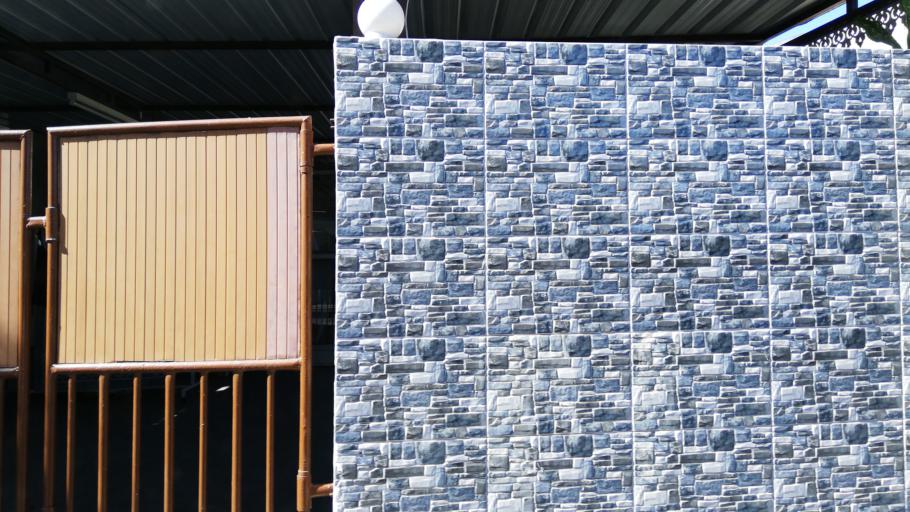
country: MU
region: Plaines Wilhems
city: Ebene
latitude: -20.2363
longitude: 57.4763
